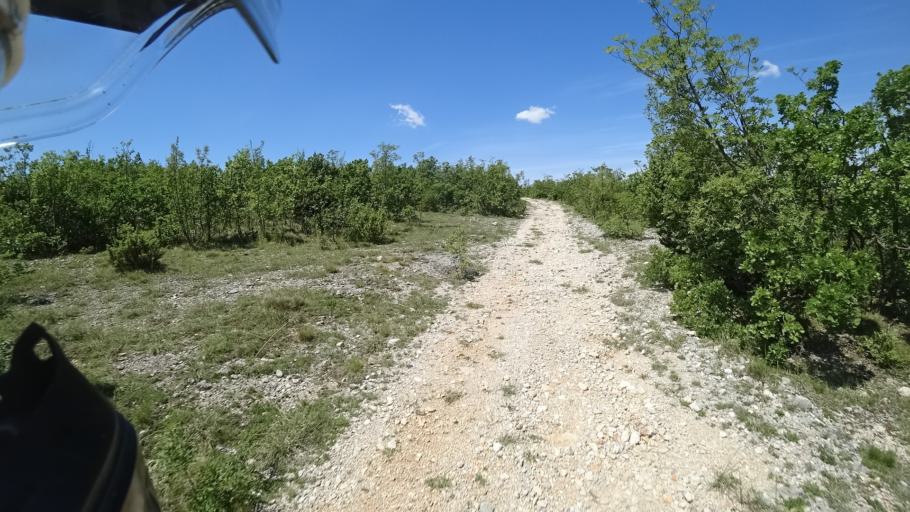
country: HR
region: Sibensko-Kniniska
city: Knin
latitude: 44.0144
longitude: 16.3306
